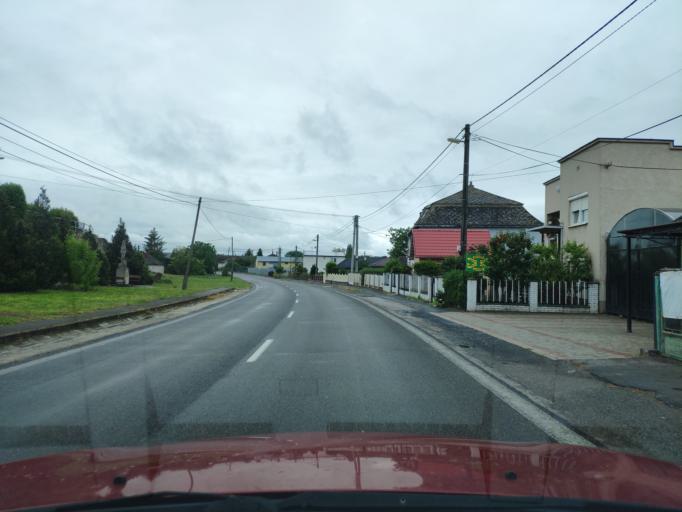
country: HU
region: Borsod-Abauj-Zemplen
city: Ricse
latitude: 48.4352
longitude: 21.9234
